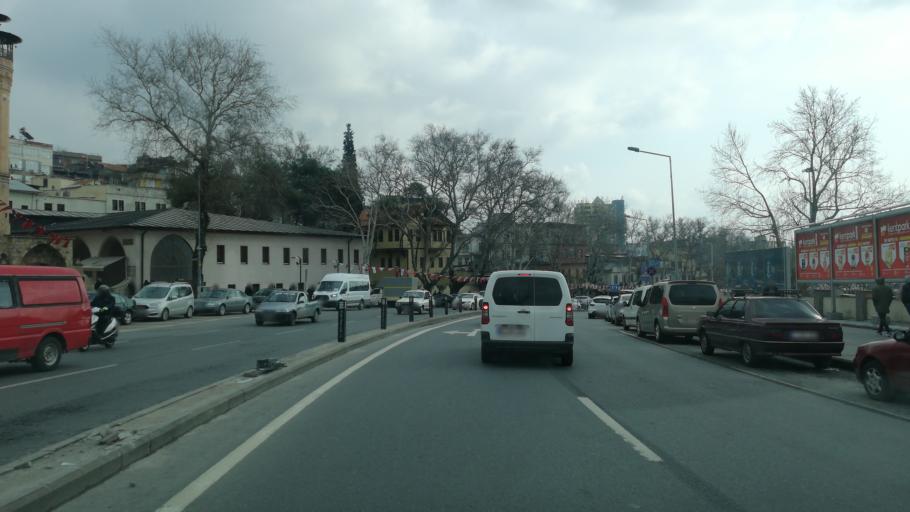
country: TR
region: Kahramanmaras
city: Kahramanmaras
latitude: 37.5849
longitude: 36.9263
